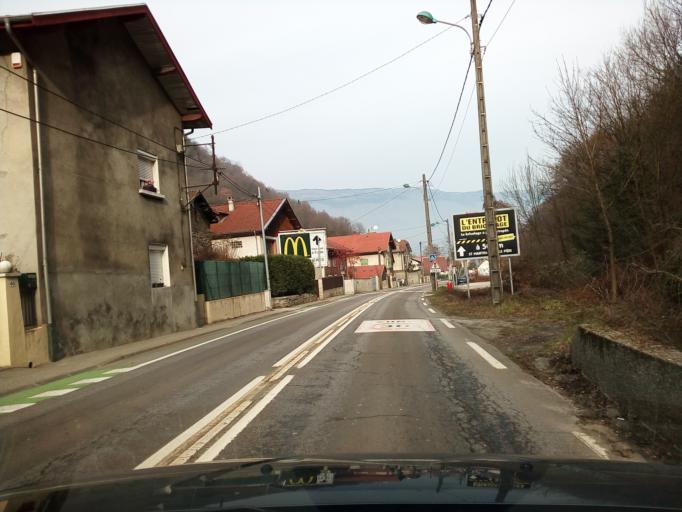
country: FR
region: Rhone-Alpes
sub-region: Departement de l'Isere
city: Gieres
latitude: 45.1728
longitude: 5.7899
